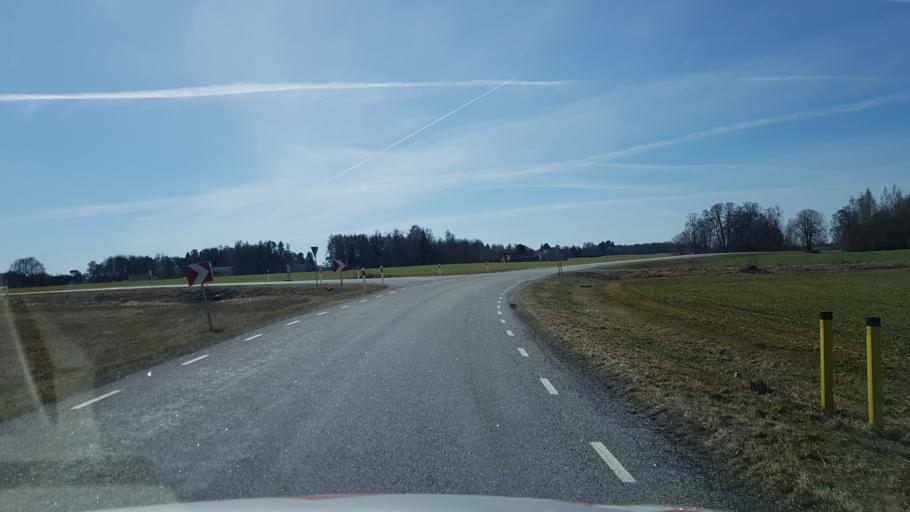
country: EE
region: Laeaene-Virumaa
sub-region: Vinni vald
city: Vinni
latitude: 59.2811
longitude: 26.3868
